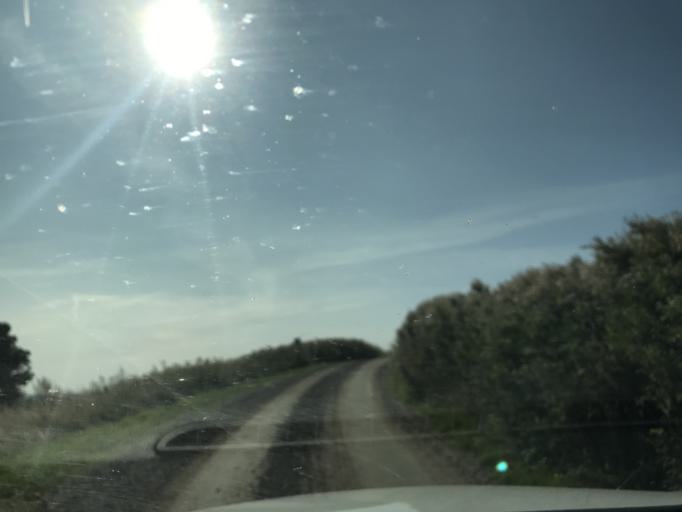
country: SE
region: Skane
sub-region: Landskrona
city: Asmundtorp
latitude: 55.9055
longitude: 12.9497
